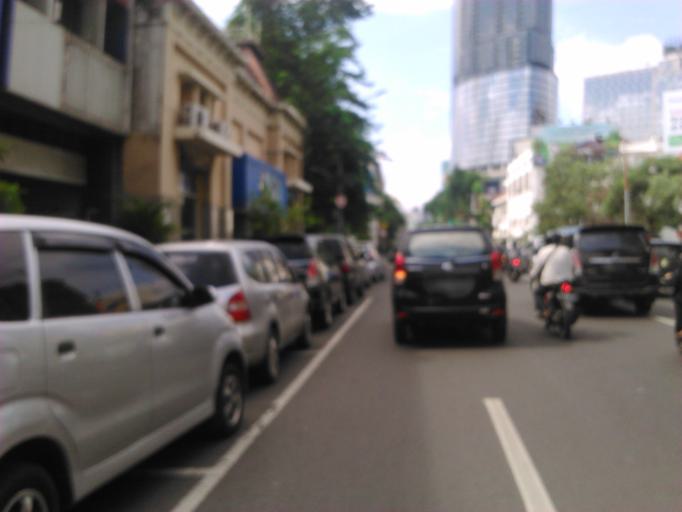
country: ID
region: East Java
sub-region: Kota Surabaya
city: Surabaya
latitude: -7.2583
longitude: 112.7383
